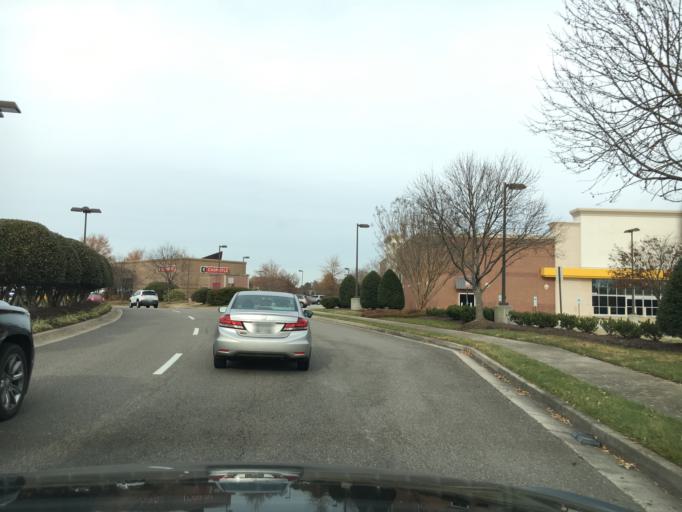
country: US
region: Virginia
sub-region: Henrico County
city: Short Pump
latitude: 37.6528
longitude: -77.6157
